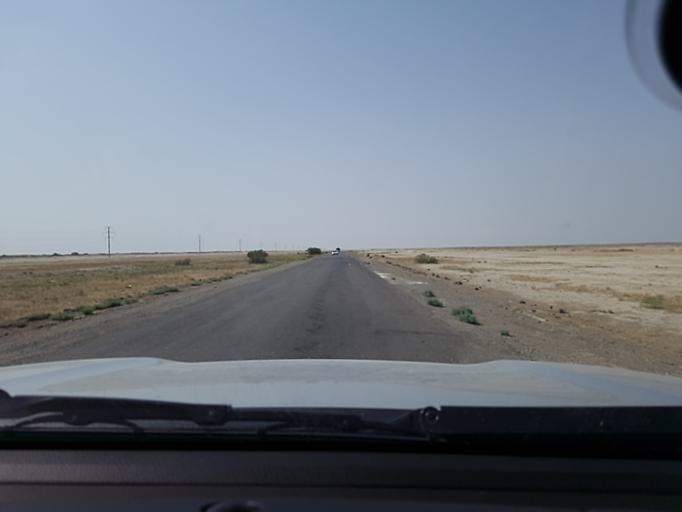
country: TM
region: Balkan
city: Gumdag
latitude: 38.8332
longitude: 54.5964
